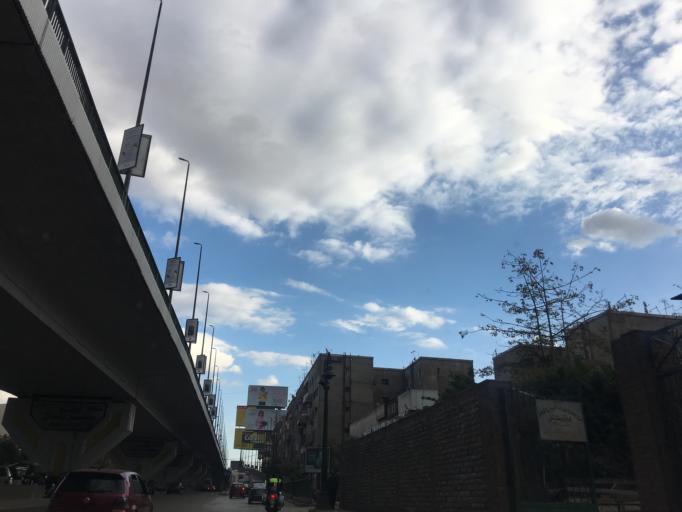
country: EG
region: Muhafazat al Qahirah
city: Cairo
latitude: 30.0644
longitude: 31.2969
